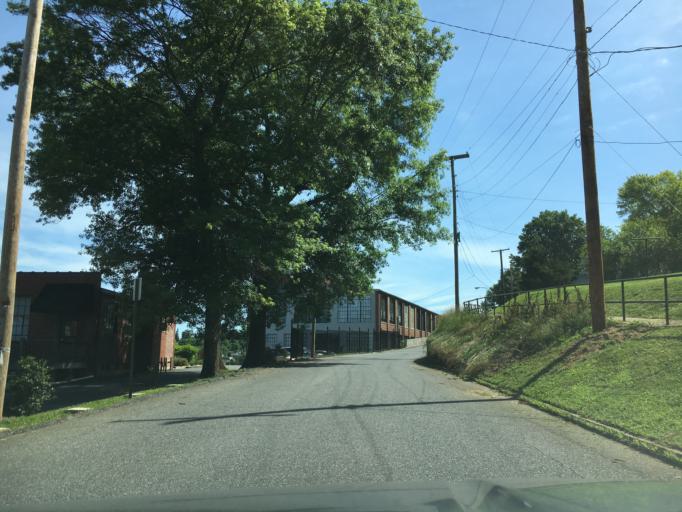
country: US
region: Virginia
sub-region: City of Lynchburg
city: West Lynchburg
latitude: 37.3974
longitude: -79.1639
